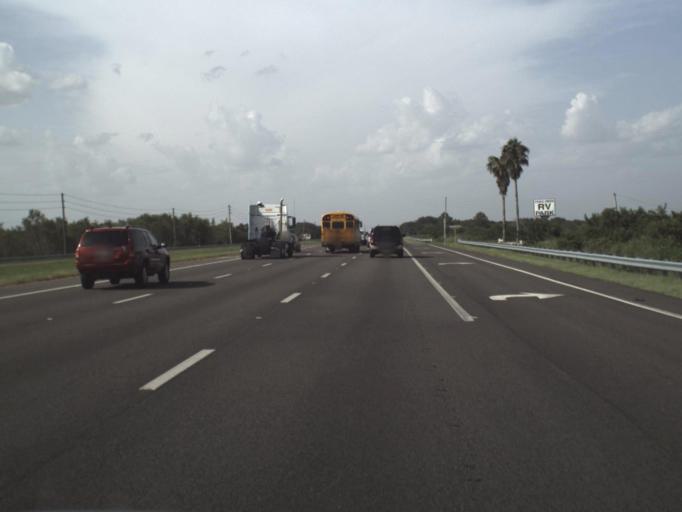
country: US
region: Florida
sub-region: Polk County
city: Dundee
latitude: 27.9907
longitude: -81.6310
